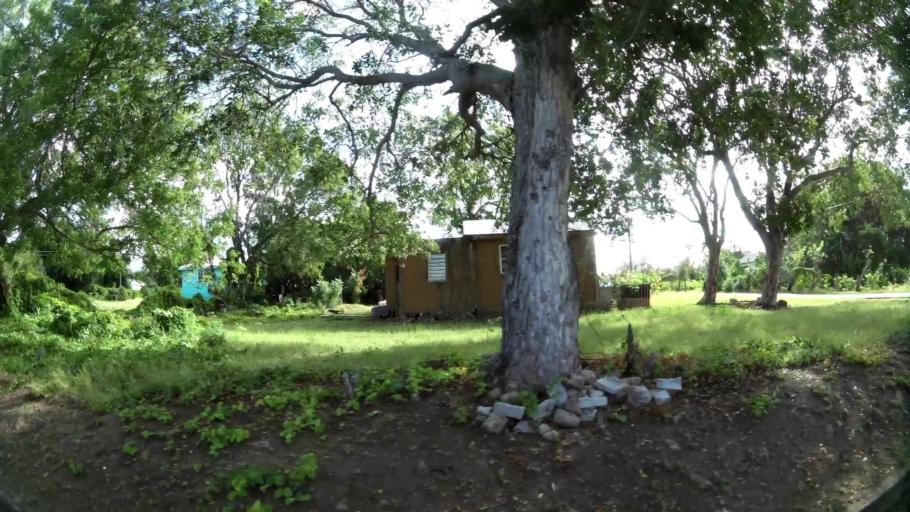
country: KN
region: Saint Paul Charlestown
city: Charlestown
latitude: 17.1296
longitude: -62.6296
